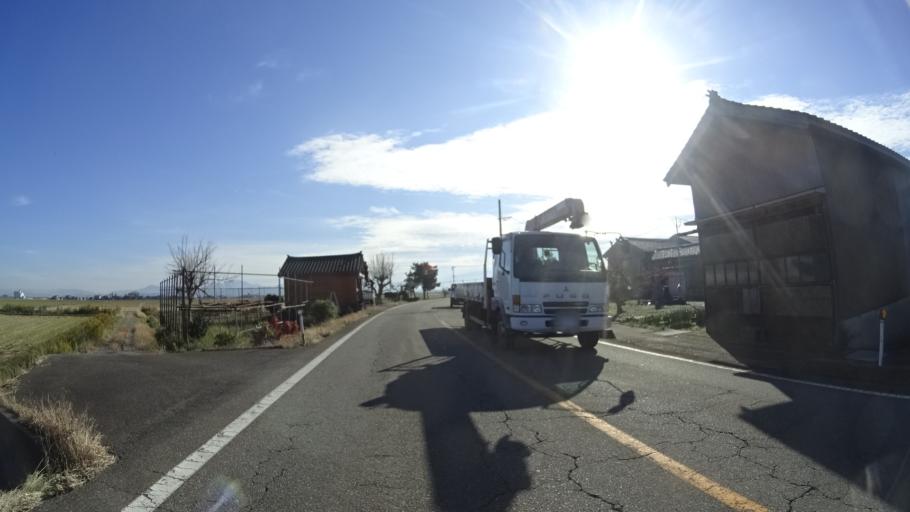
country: JP
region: Niigata
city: Mitsuke
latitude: 37.5748
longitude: 138.8400
